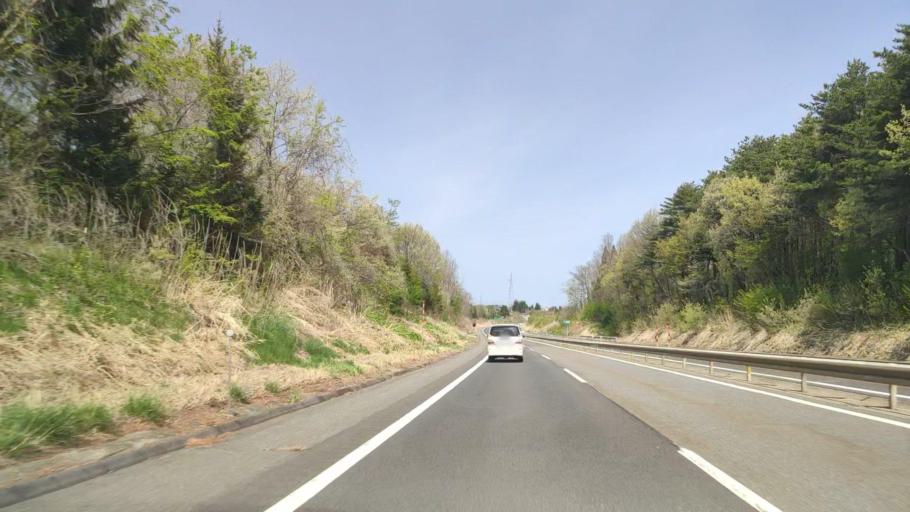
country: JP
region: Aomori
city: Hachinohe
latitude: 40.4723
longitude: 141.4611
